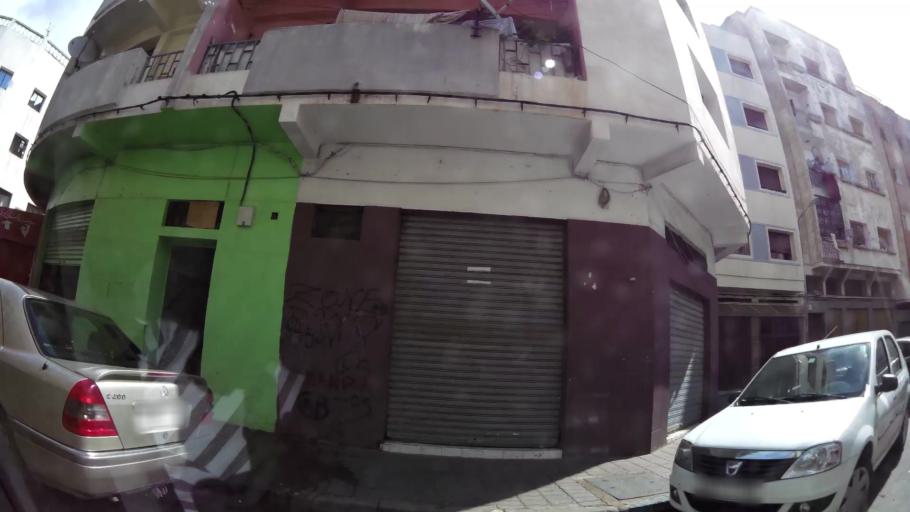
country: MA
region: Grand Casablanca
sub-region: Casablanca
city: Casablanca
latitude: 33.5827
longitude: -7.5801
